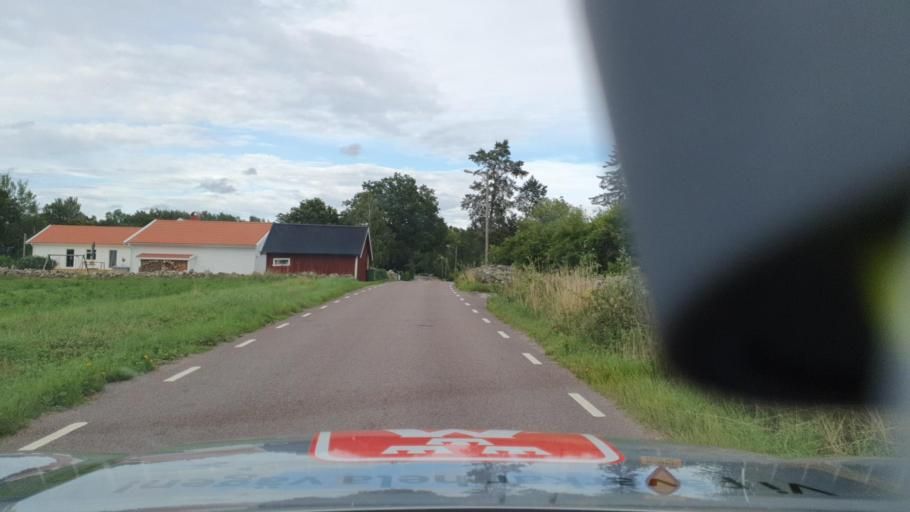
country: SE
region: Kalmar
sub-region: Kalmar Kommun
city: Lindsdal
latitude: 56.7807
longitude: 16.2780
